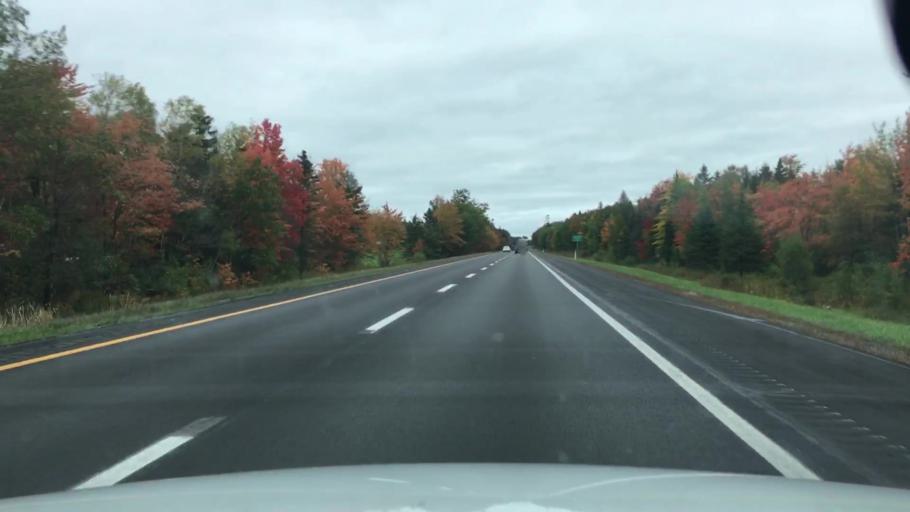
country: US
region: Maine
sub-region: Penobscot County
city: Veazie
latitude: 44.8473
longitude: -68.7291
